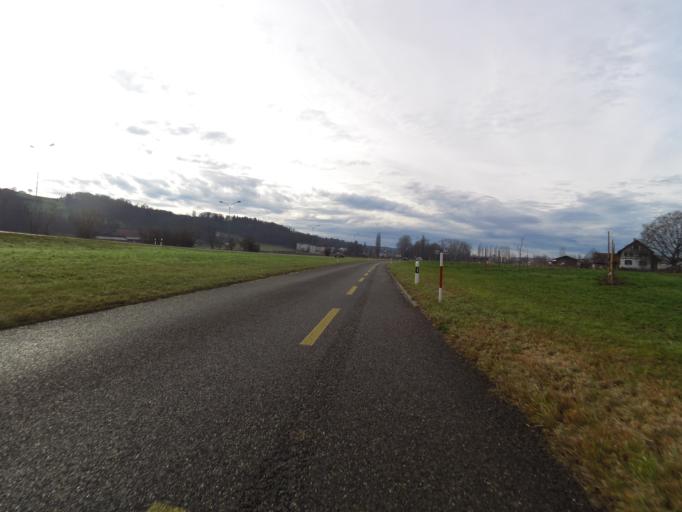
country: CH
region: Thurgau
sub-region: Frauenfeld District
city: Frauenfeld
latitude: 47.5712
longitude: 8.9261
